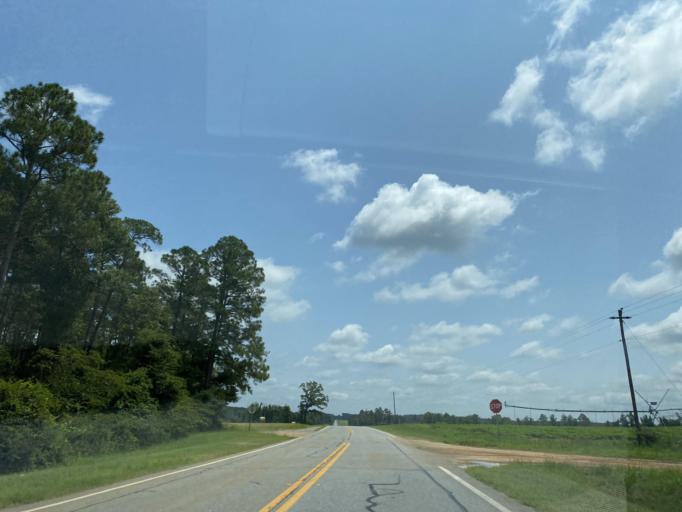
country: US
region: Georgia
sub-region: Wilcox County
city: Abbeville
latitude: 32.0026
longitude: -83.1410
